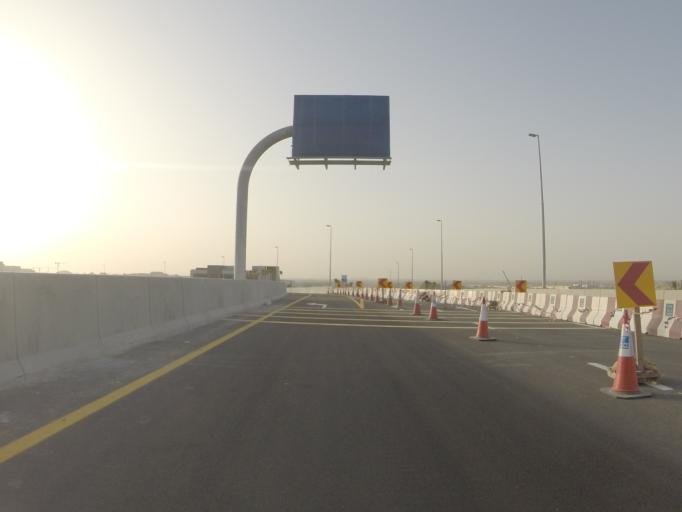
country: AE
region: Dubai
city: Dubai
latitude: 24.9218
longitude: 54.9953
